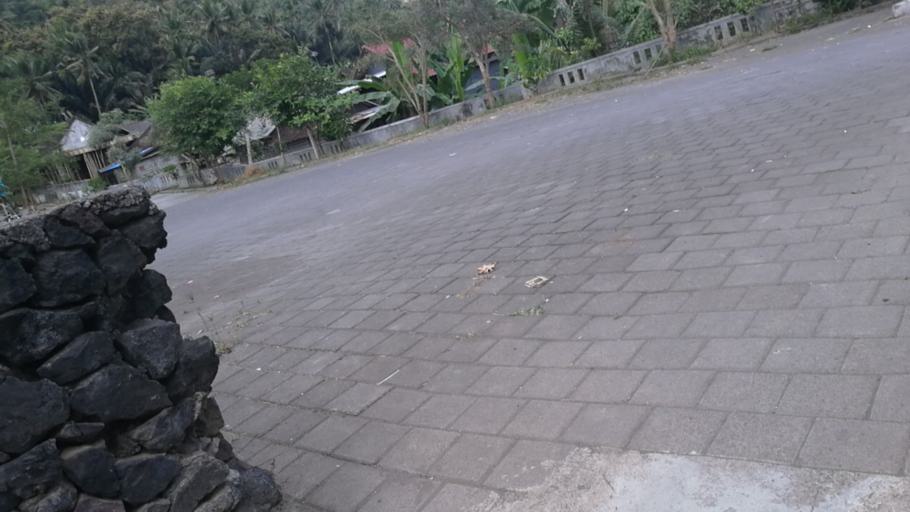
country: ID
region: Bali
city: Banjar Pegeringsingan
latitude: -8.4773
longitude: 115.5666
